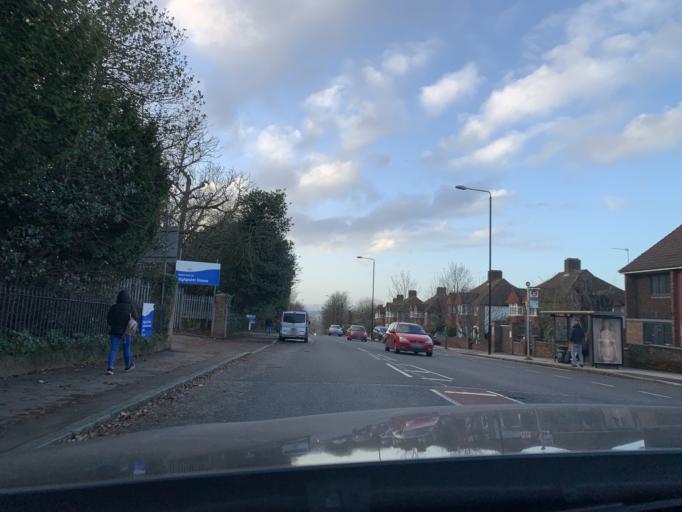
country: GB
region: England
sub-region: Greater London
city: Woolwich
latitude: 51.4693
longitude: 0.0659
